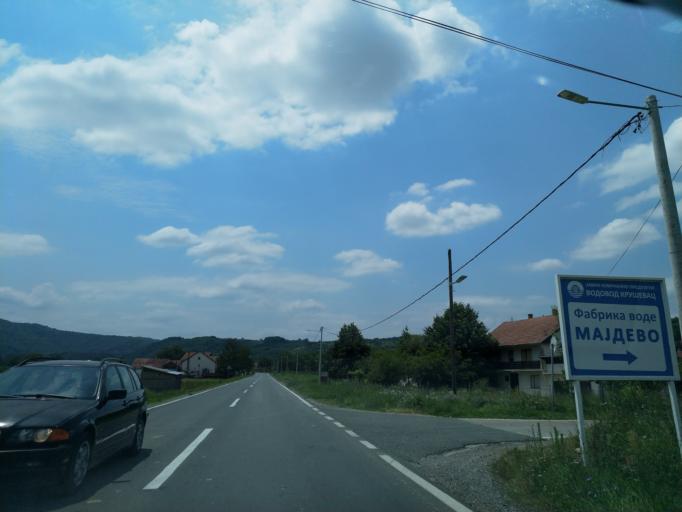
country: RS
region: Central Serbia
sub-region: Toplicki Okrug
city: Blace
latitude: 43.4358
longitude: 21.2150
